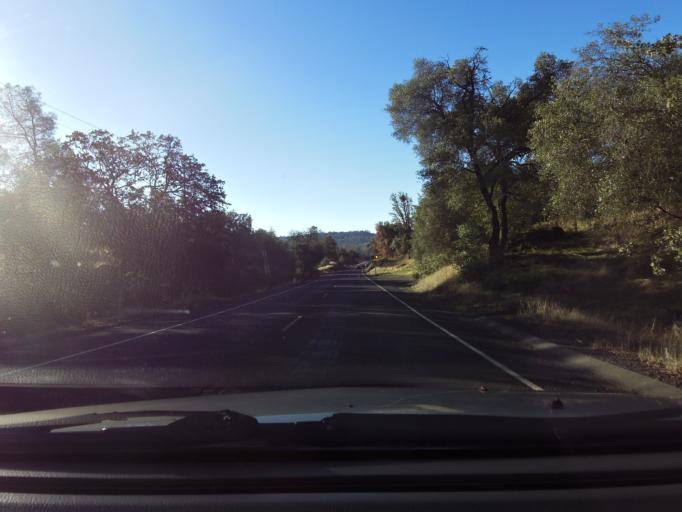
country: US
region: California
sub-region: Madera County
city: Coarsegold
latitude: 37.2238
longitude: -119.7076
